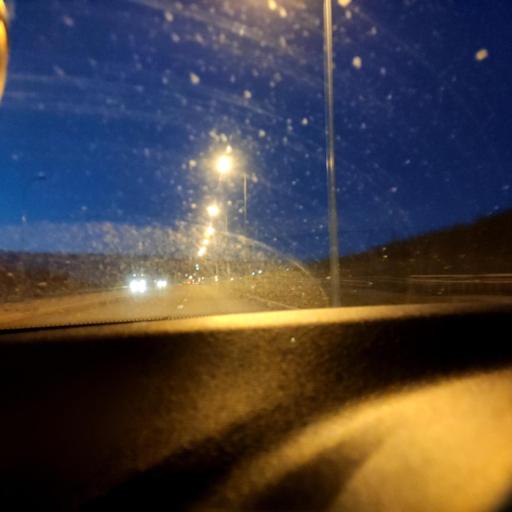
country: RU
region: Samara
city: Petra-Dubrava
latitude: 53.3034
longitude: 50.3132
